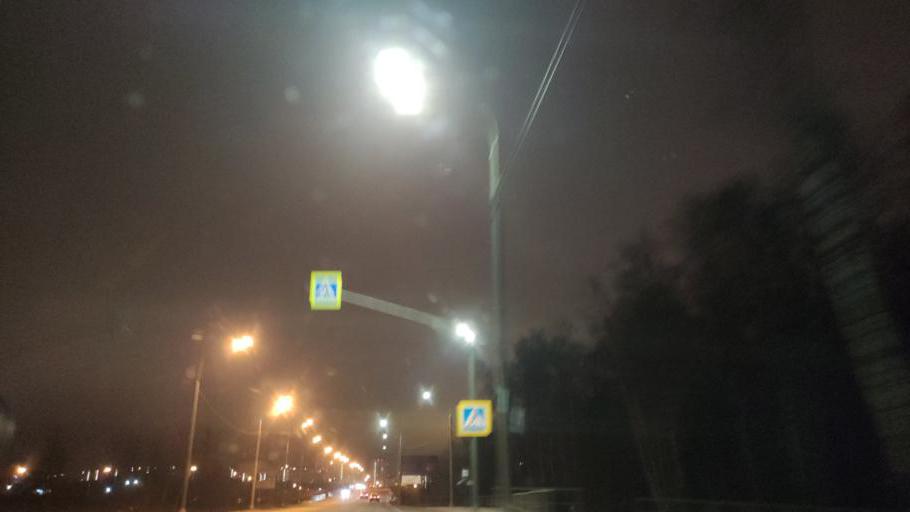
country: RU
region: Moskovskaya
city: Moskovskiy
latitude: 55.6132
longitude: 37.3484
